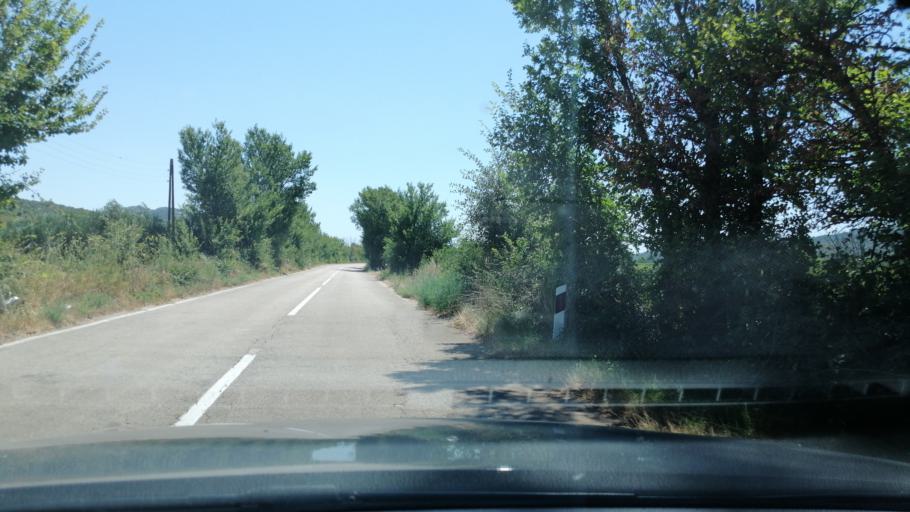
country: HR
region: Sibensko-Kniniska
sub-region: Grad Sibenik
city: Pirovac
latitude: 43.8828
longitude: 15.6729
